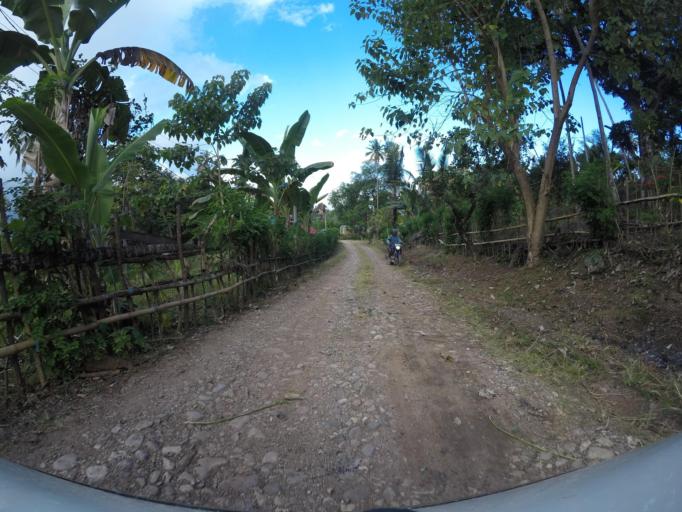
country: TL
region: Baucau
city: Venilale
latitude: -8.6877
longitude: 126.6675
